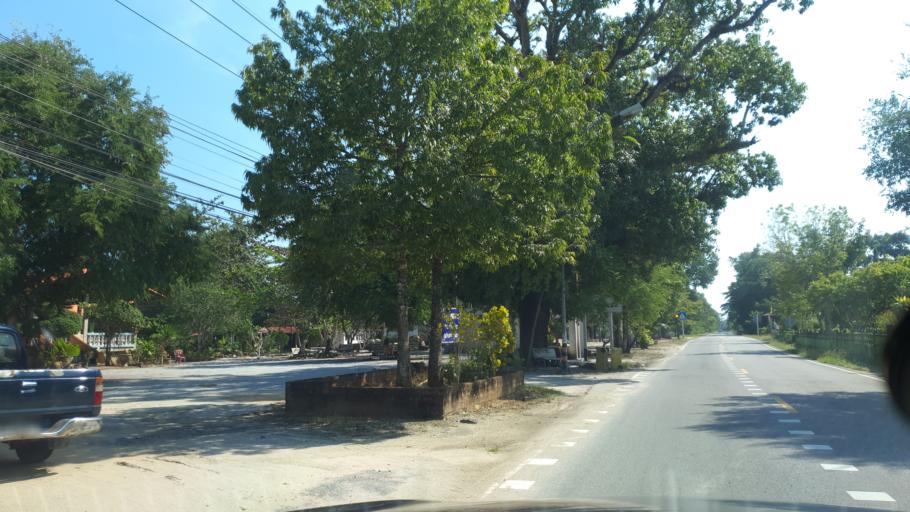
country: TH
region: Surat Thani
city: Tha Chana
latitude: 9.5863
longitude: 99.2021
